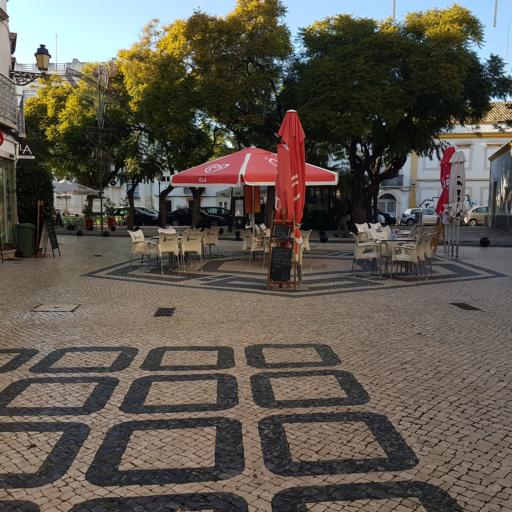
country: PT
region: Faro
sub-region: Faro
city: Faro
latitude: 37.0171
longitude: -7.9328
